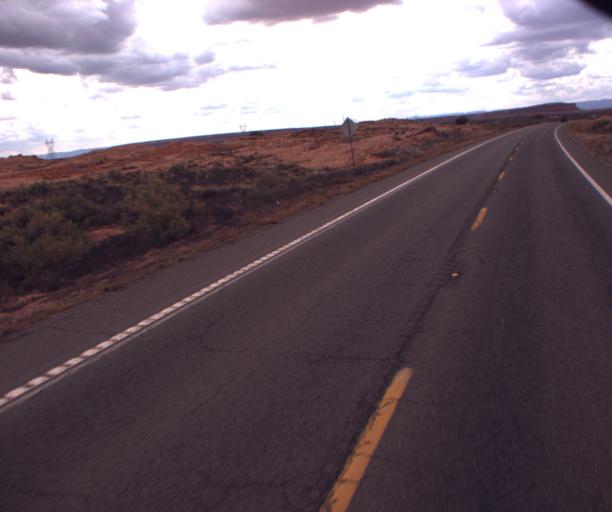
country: US
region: Arizona
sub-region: Navajo County
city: Kayenta
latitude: 36.8242
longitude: -109.8683
